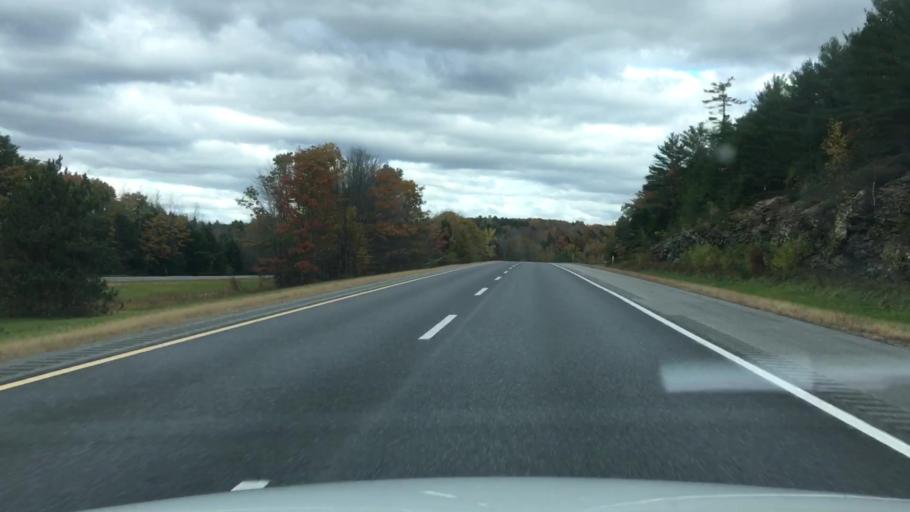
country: US
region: Maine
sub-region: Sagadahoc County
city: Topsham
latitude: 43.9887
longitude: -69.9400
